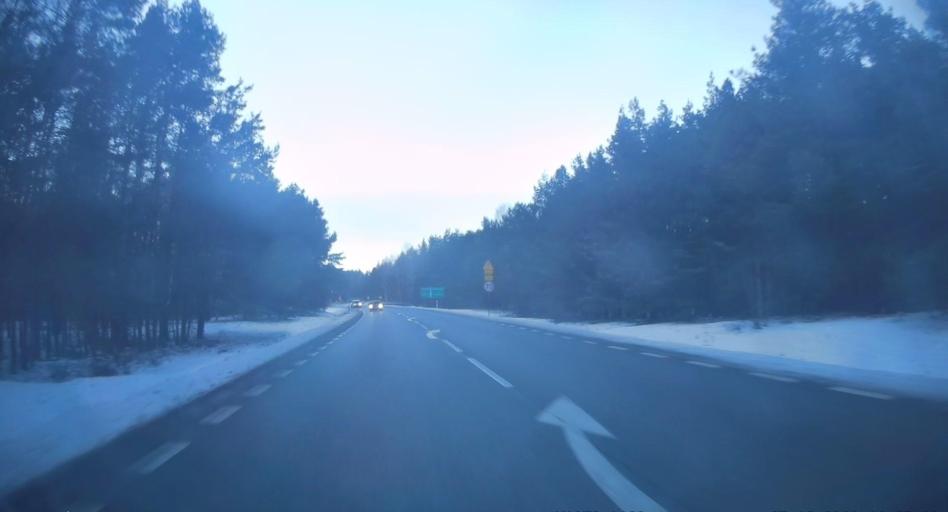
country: PL
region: Swietokrzyskie
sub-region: Powiat konecki
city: Ruda Maleniecka
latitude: 51.1421
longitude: 20.2462
